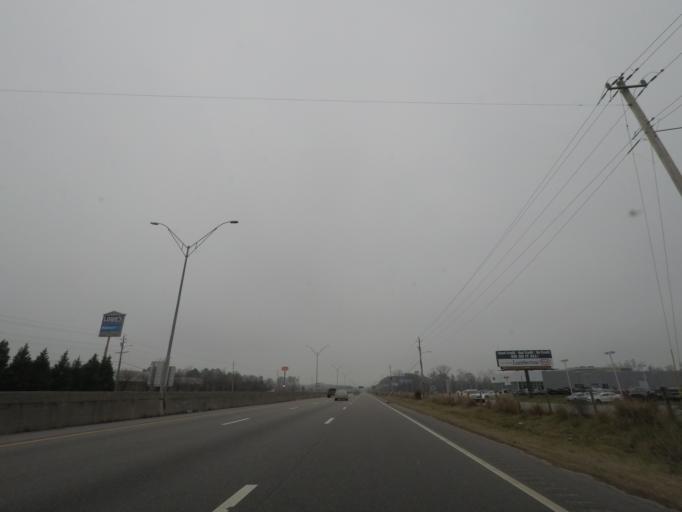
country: US
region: North Carolina
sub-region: Robeson County
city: Lumberton
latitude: 34.6659
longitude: -79.0075
